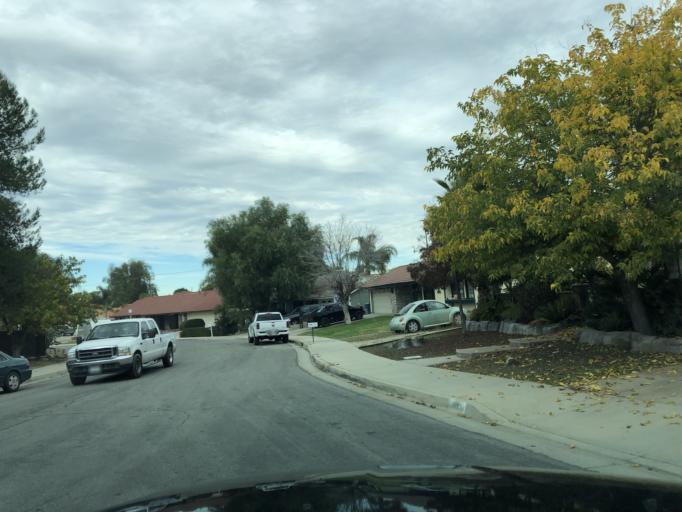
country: US
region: California
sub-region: Riverside County
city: Wildomar
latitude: 33.6222
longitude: -117.2702
